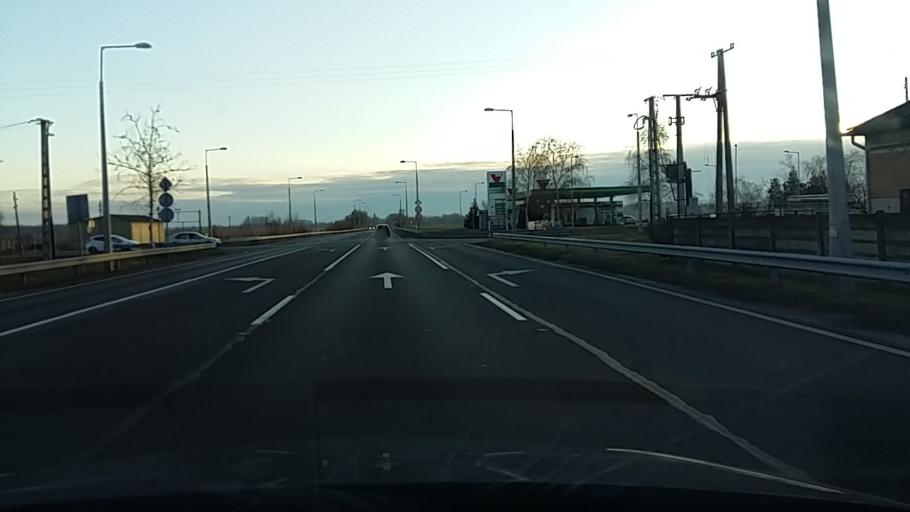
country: HU
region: Hajdu-Bihar
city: Teglas
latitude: 47.7098
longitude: 21.6594
